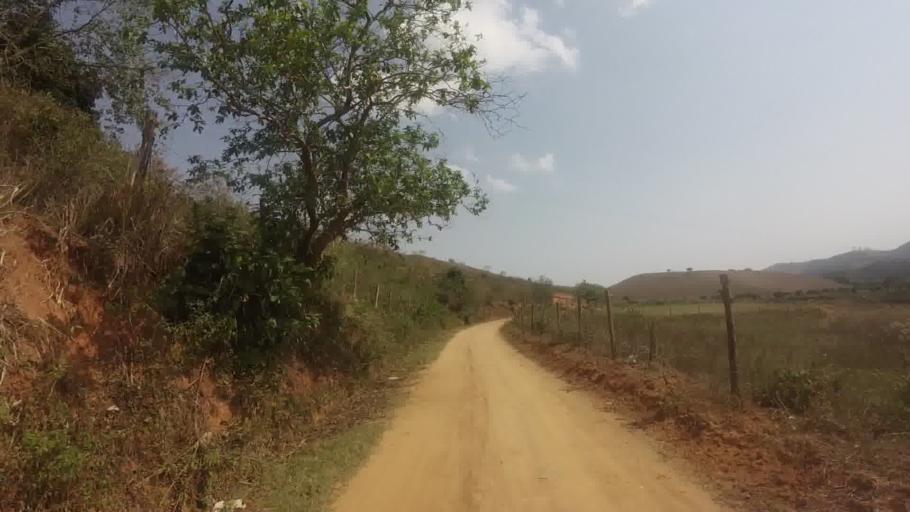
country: BR
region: Espirito Santo
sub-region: Sao Jose Do Calcado
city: Sao Jose do Calcado
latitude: -21.0307
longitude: -41.5178
